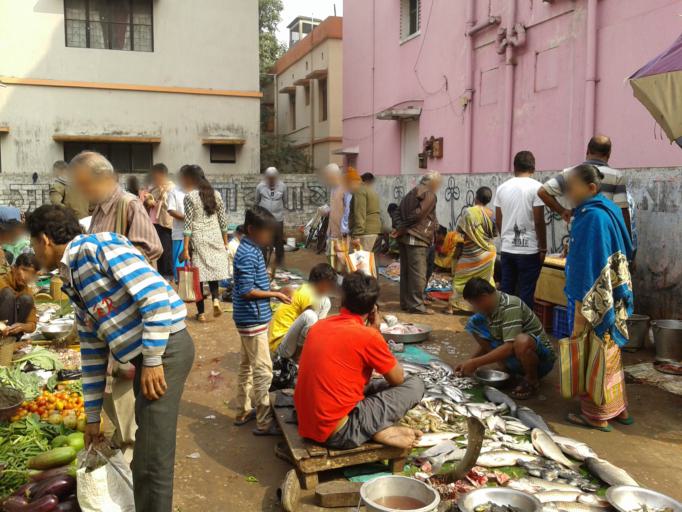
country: IN
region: West Bengal
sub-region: Kolkata
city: Kolkata
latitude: 22.5107
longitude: 88.3825
